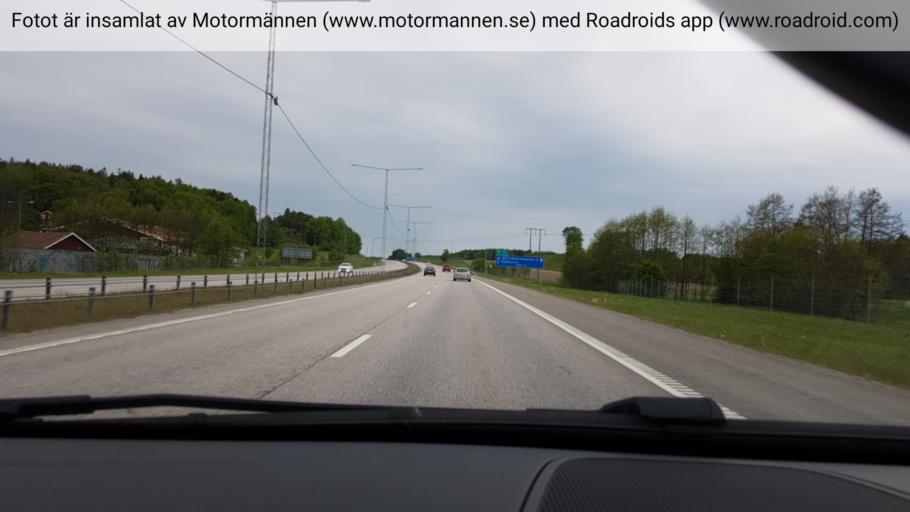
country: SE
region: Stockholm
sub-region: Haninge Kommun
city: Jordbro
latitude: 59.1310
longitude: 18.1444
